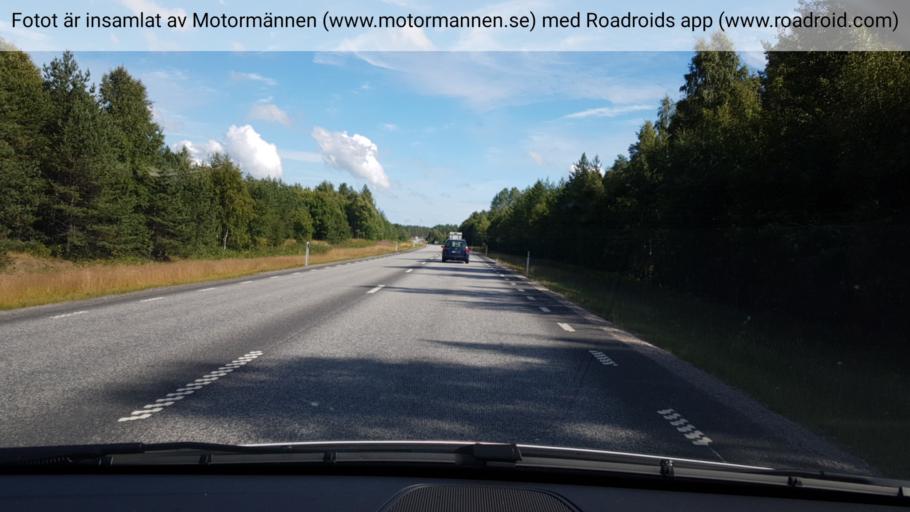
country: SE
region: Vaesterbotten
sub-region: Umea Kommun
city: Roback
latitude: 63.8482
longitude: 20.1305
